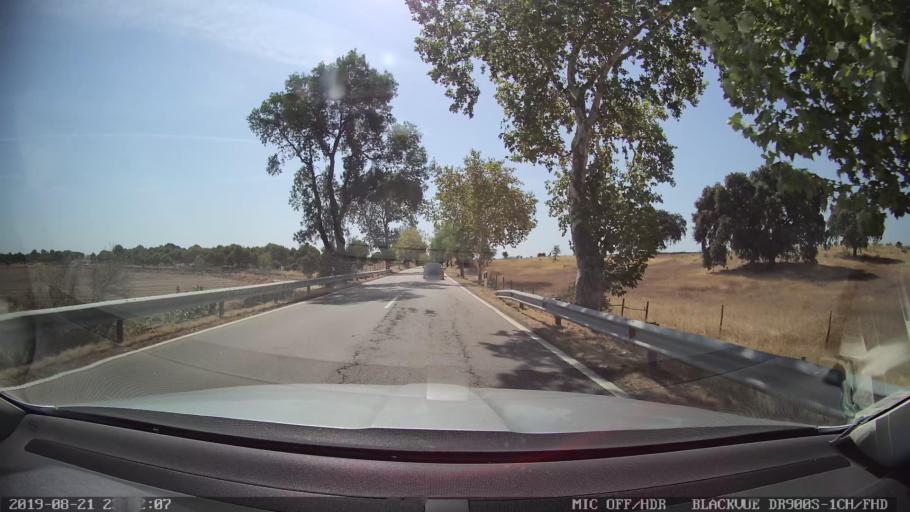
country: PT
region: Castelo Branco
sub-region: Idanha-A-Nova
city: Idanha-a-Nova
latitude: 39.8592
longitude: -7.3148
